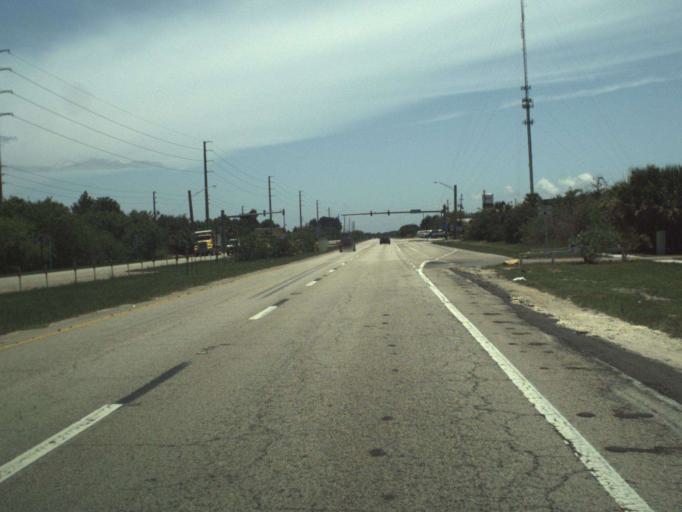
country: US
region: Florida
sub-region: Saint Lucie County
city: Lakewood Park
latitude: 27.5506
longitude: -80.3694
